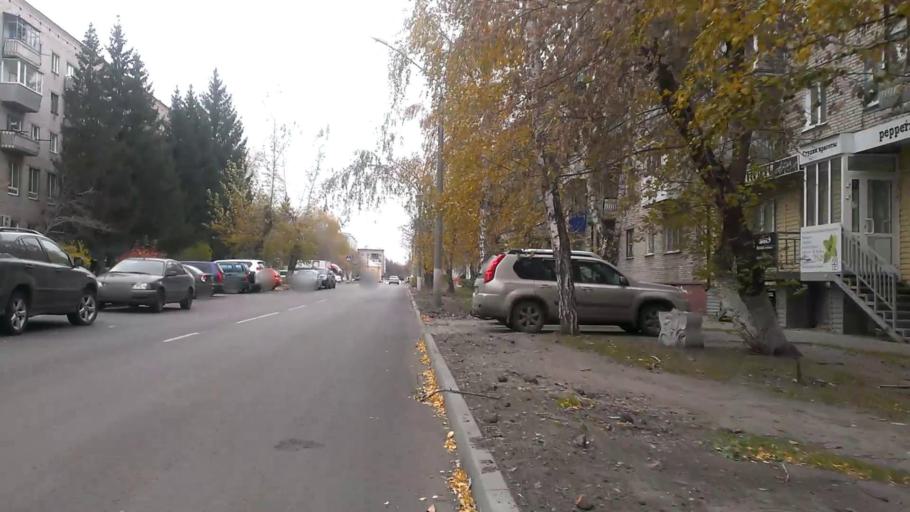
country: RU
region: Altai Krai
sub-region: Gorod Barnaulskiy
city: Barnaul
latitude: 53.3505
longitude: 83.7703
